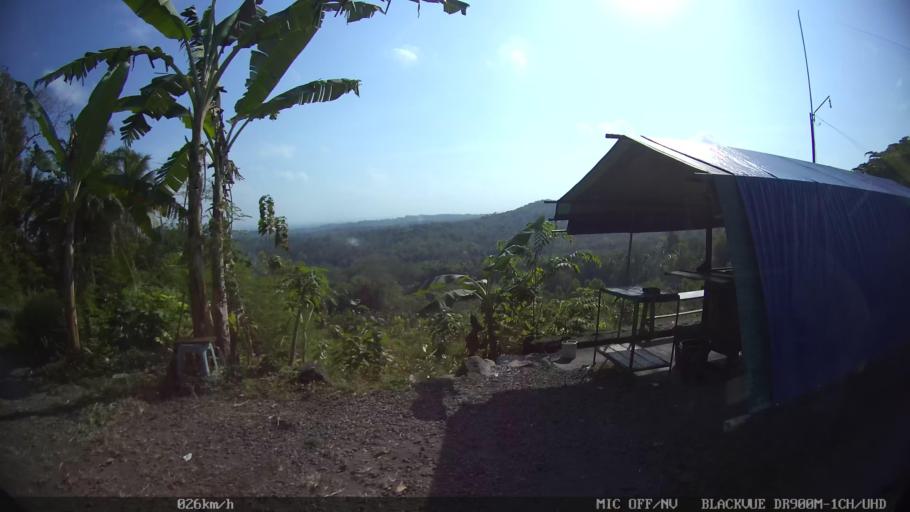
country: ID
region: Daerah Istimewa Yogyakarta
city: Kasihan
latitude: -7.8349
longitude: 110.2773
